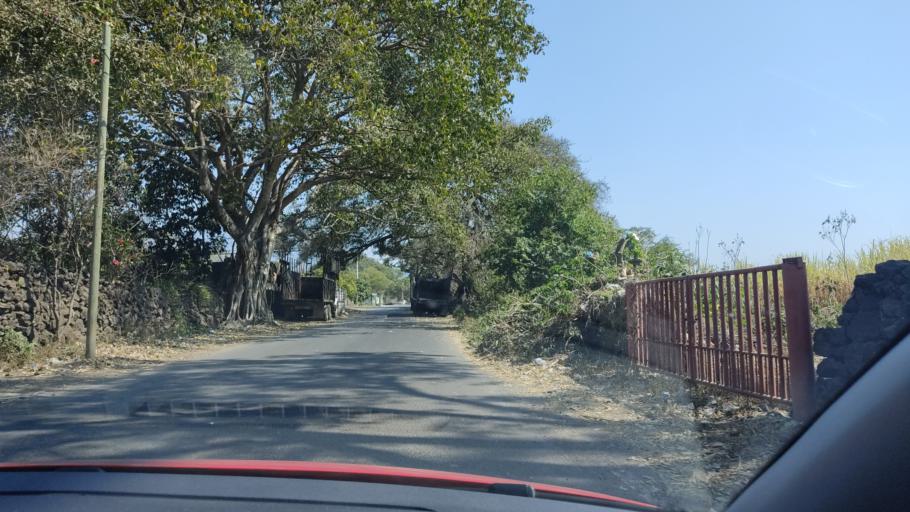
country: MX
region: Nayarit
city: Puga
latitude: 21.5321
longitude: -104.8079
